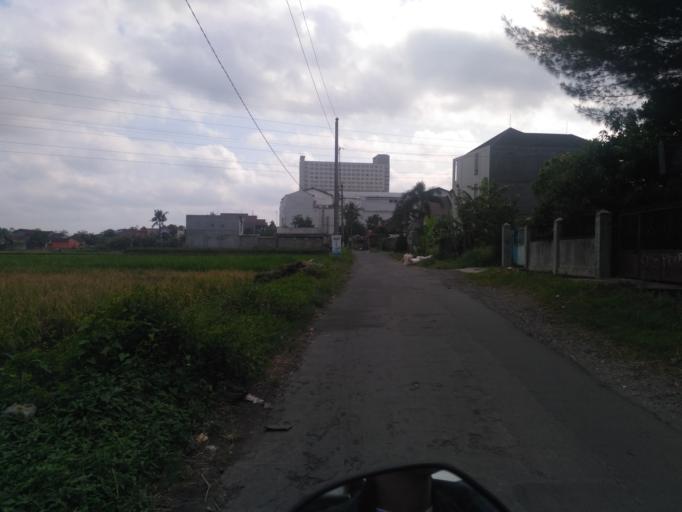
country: ID
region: Daerah Istimewa Yogyakarta
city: Yogyakarta
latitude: -7.7576
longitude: 110.3593
